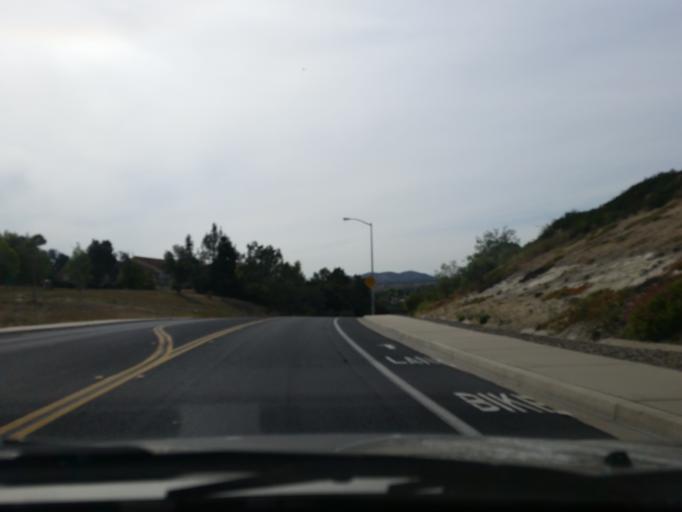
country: US
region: California
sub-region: San Luis Obispo County
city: Arroyo Grande
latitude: 35.1346
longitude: -120.5855
